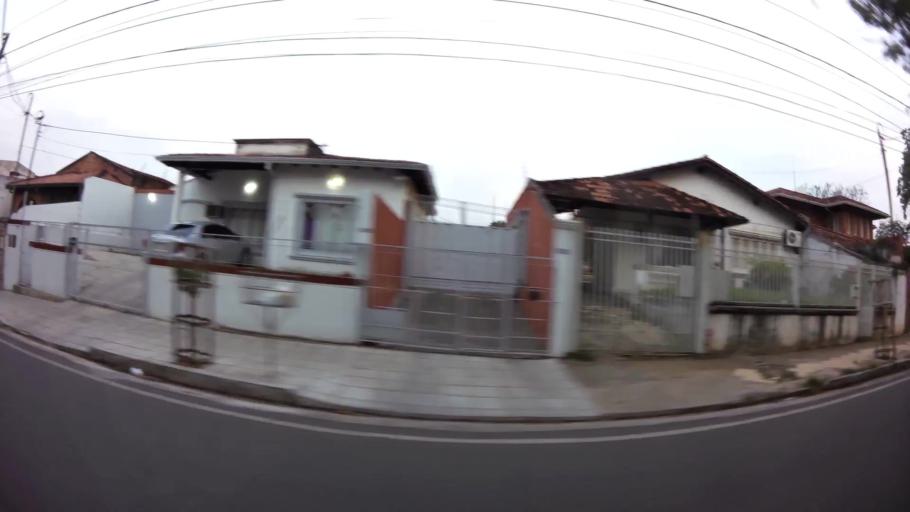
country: PY
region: Asuncion
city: Asuncion
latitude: -25.3150
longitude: -57.6188
